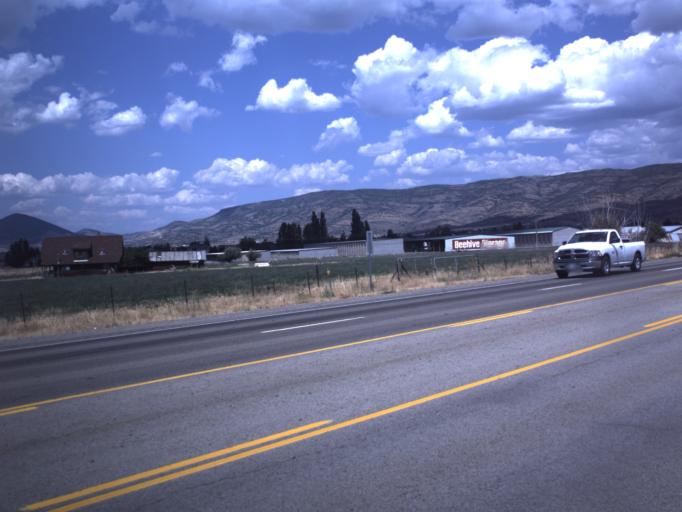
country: US
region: Utah
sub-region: Wasatch County
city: Heber
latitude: 40.4867
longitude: -111.4231
